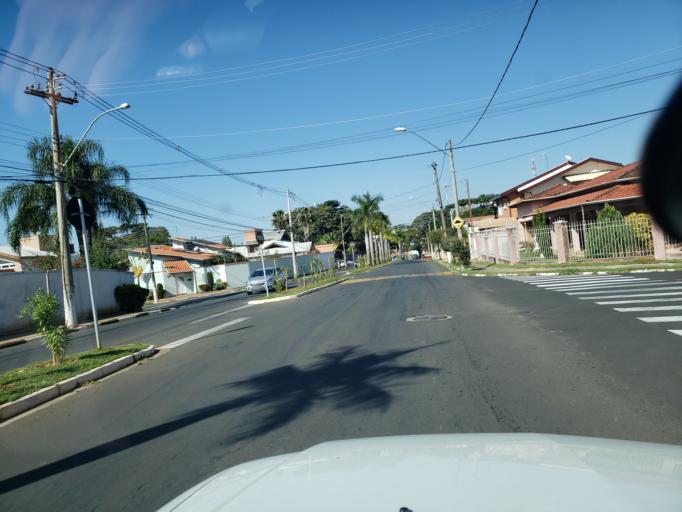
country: BR
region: Sao Paulo
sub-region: Itapira
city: Itapira
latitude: -22.4272
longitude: -46.8365
